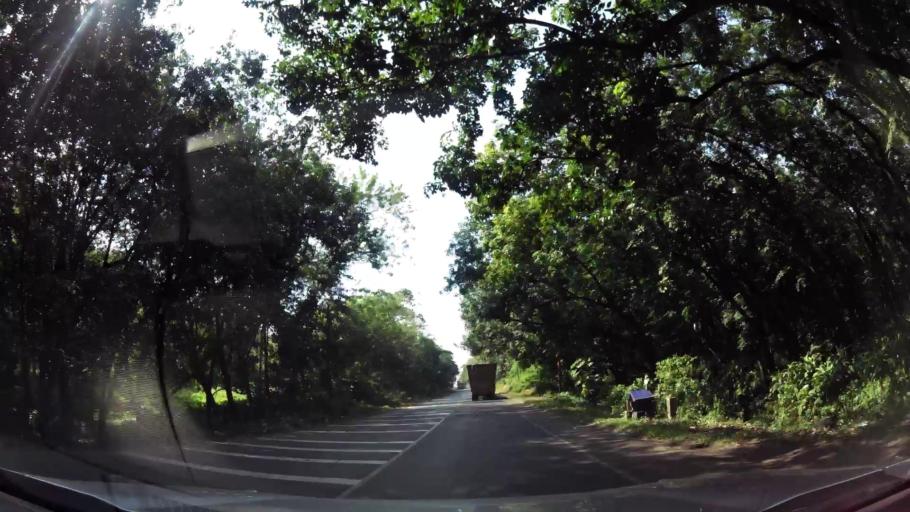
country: GT
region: Retalhuleu
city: San Sebastian
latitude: 14.5514
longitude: -91.6339
